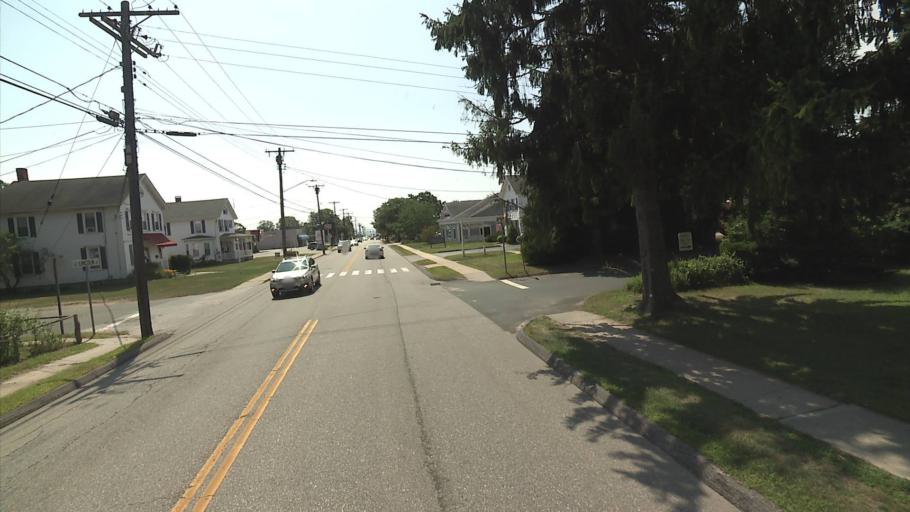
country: US
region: Connecticut
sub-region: New London County
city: Niantic
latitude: 41.3271
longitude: -72.1937
